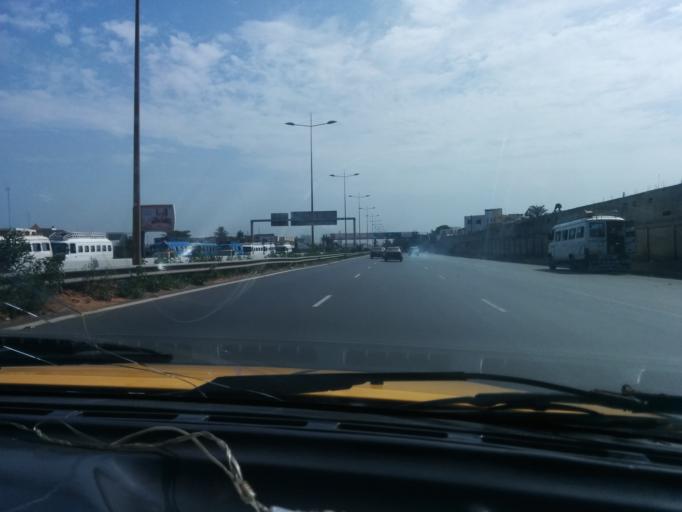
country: SN
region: Dakar
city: Dakar
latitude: 14.6957
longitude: -17.4425
